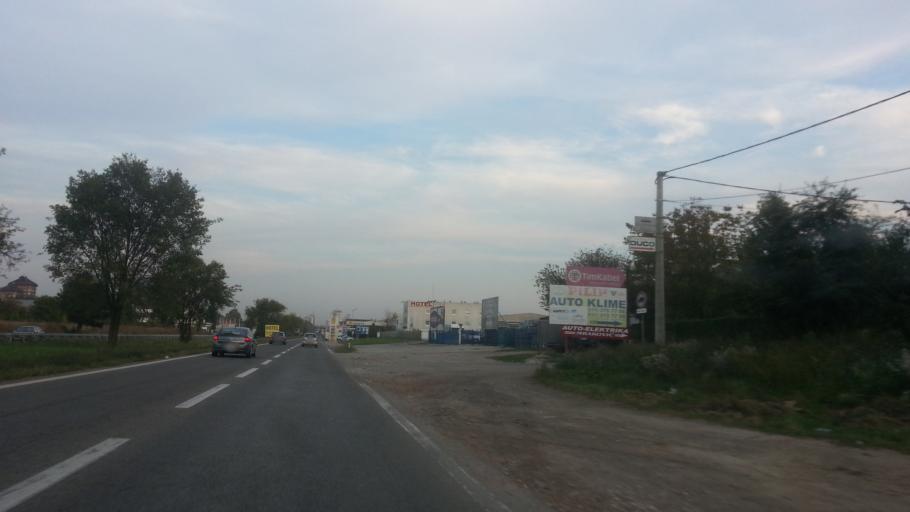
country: RS
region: Central Serbia
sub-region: Belgrade
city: Zemun
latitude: 44.8590
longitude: 20.3573
